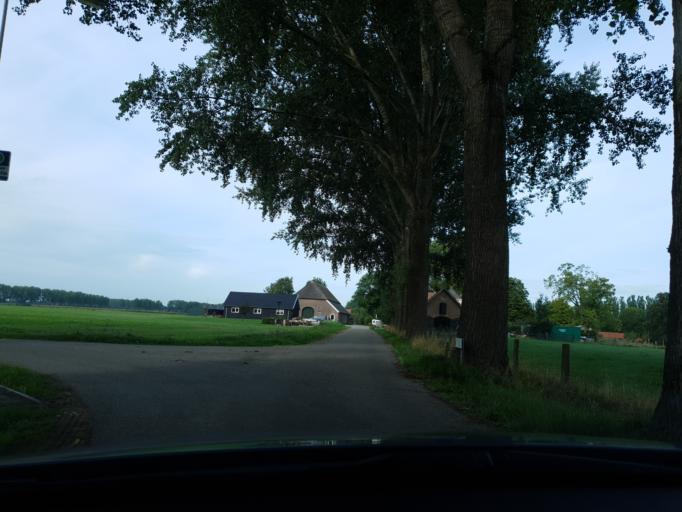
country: NL
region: Gelderland
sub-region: Gemeente Overbetuwe
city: Andelst
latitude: 51.8740
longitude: 5.7209
